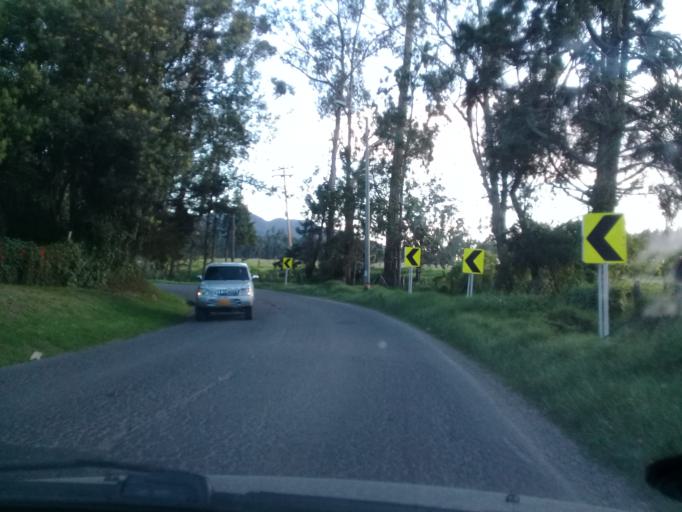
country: CO
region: Cundinamarca
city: Tenjo
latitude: 4.8529
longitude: -74.1337
